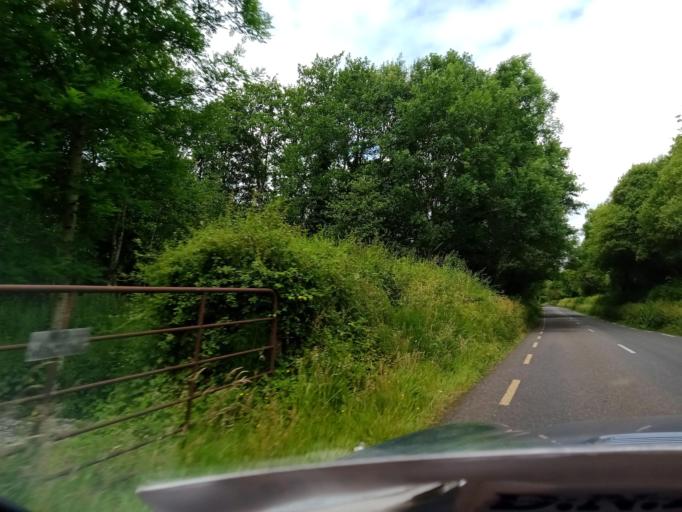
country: IE
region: Leinster
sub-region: Kilkenny
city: Piltown
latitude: 52.4687
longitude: -7.2729
